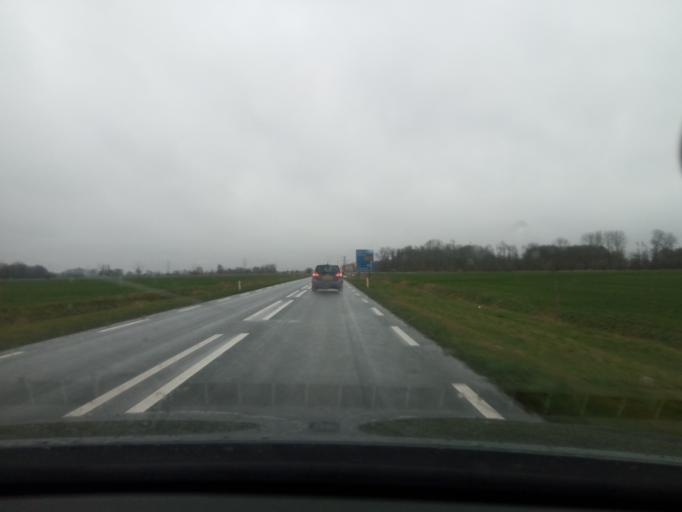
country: NL
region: Groningen
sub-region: Gemeente Appingedam
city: Appingedam
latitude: 53.3169
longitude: 6.7900
